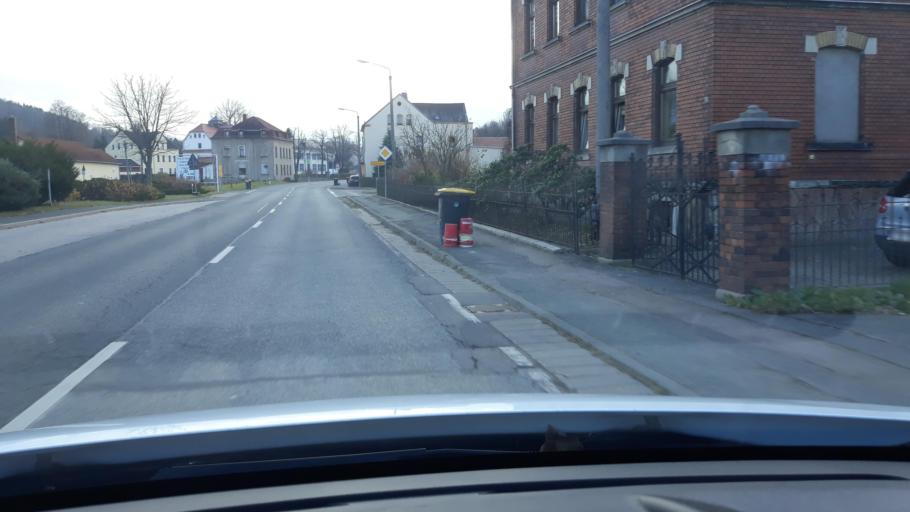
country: DE
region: Saxony
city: Kirchberg
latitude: 50.6448
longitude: 12.5157
